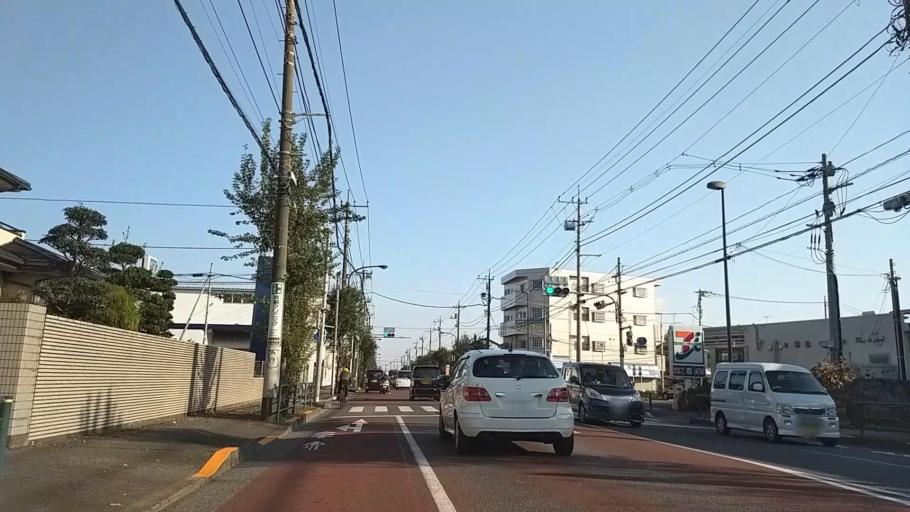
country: JP
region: Tokyo
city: Fussa
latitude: 35.7799
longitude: 139.3284
